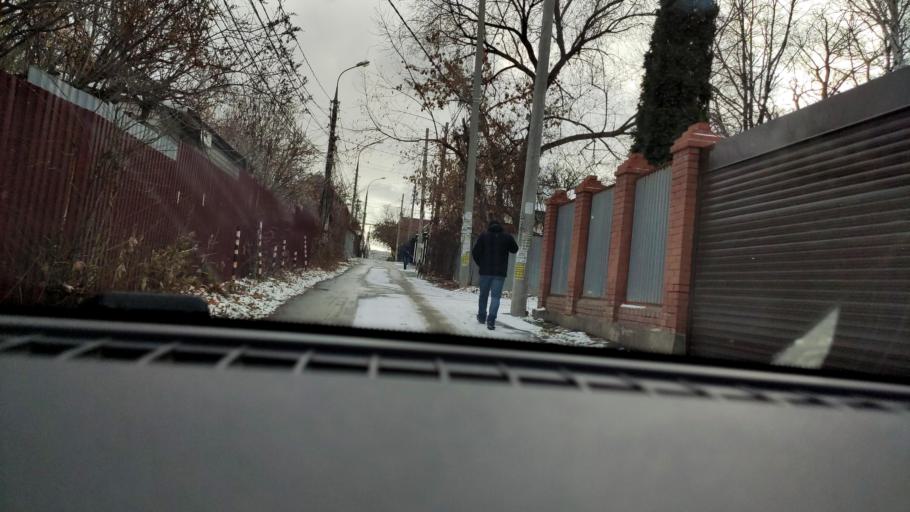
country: RU
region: Samara
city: Samara
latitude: 53.2735
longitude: 50.1987
